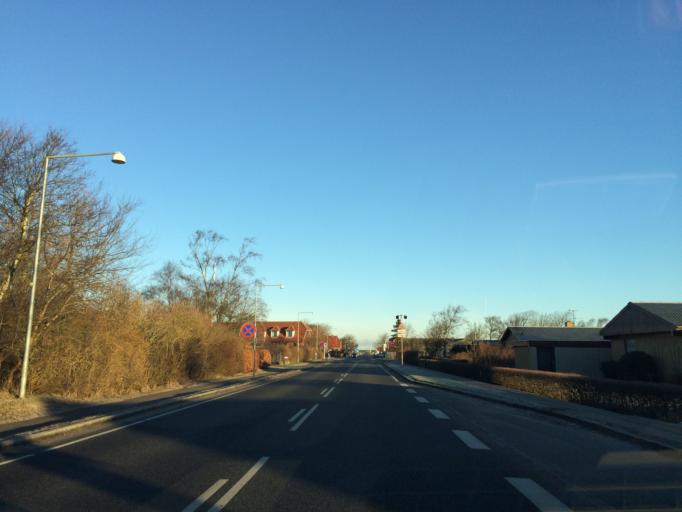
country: DK
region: Central Jutland
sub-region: Lemvig Kommune
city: Lemvig
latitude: 56.4184
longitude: 8.3070
